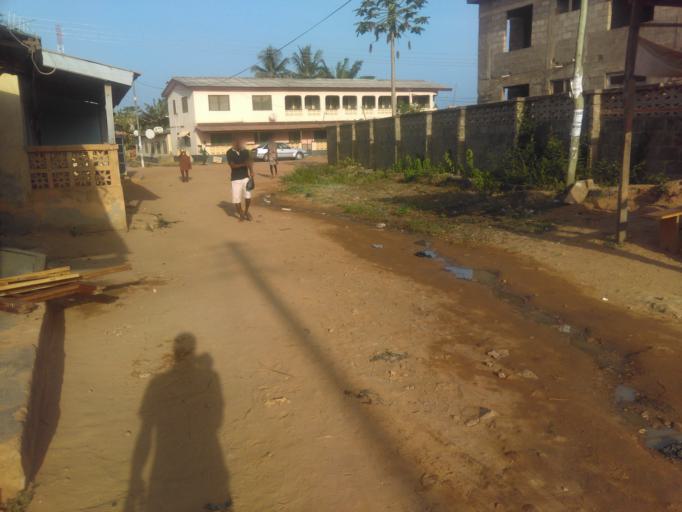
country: GH
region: Central
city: Cape Coast
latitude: 5.1099
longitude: -1.2940
